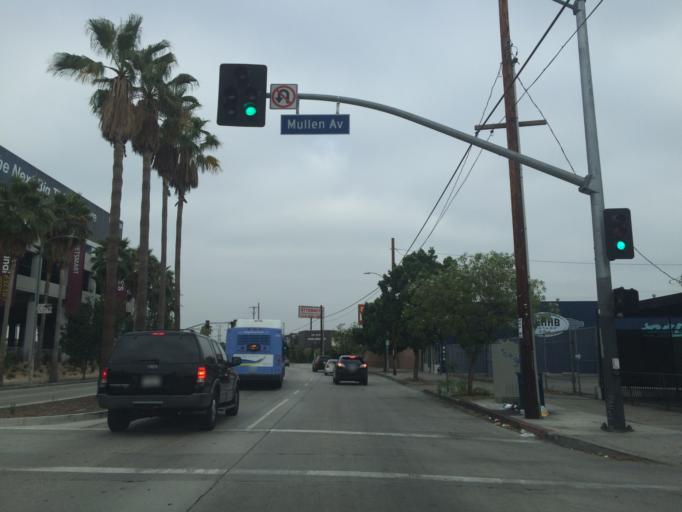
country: US
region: California
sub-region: Los Angeles County
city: West Hollywood
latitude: 34.0488
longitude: -118.3356
